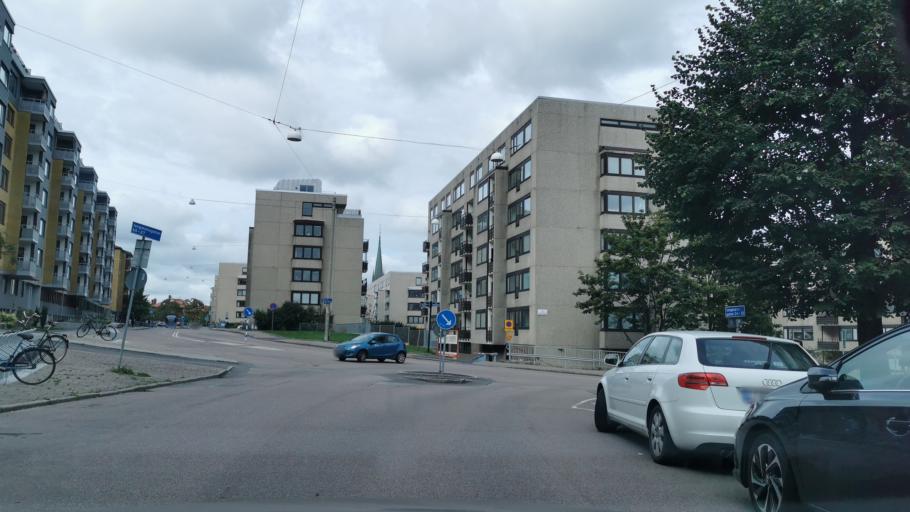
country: SE
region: Vaestra Goetaland
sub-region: Goteborg
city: Goeteborg
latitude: 57.6936
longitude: 11.9467
